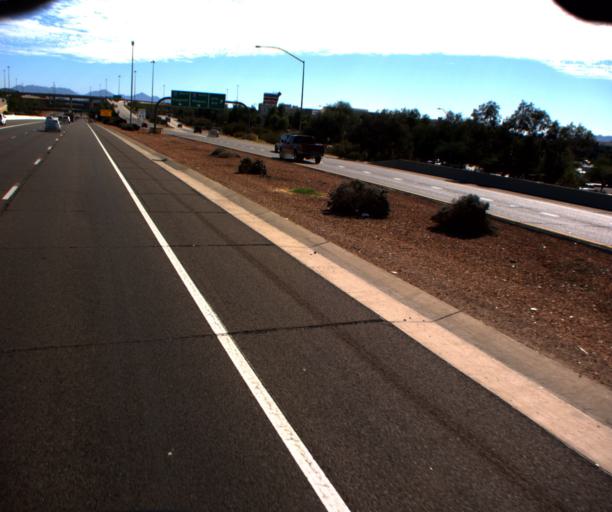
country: US
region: Arizona
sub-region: Maricopa County
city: Peoria
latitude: 33.6686
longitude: -112.1246
